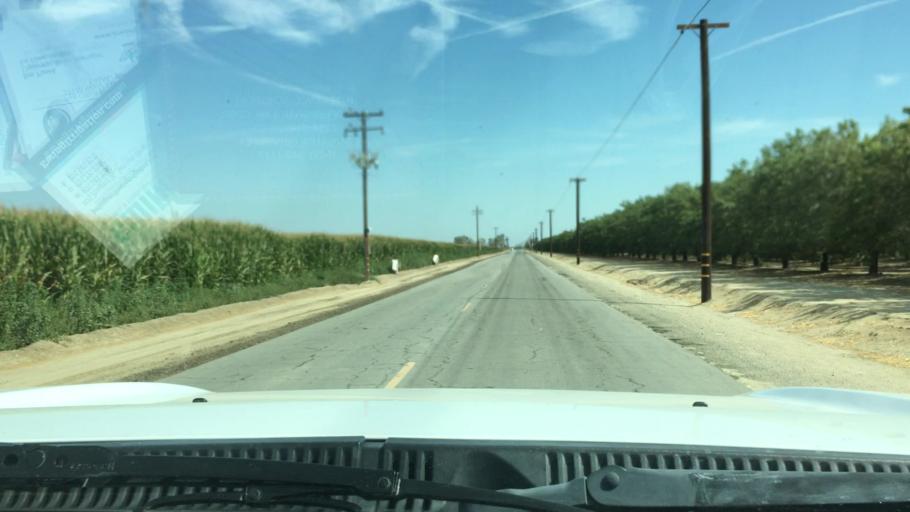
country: US
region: California
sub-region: Kern County
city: Buttonwillow
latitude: 35.4214
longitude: -119.3763
